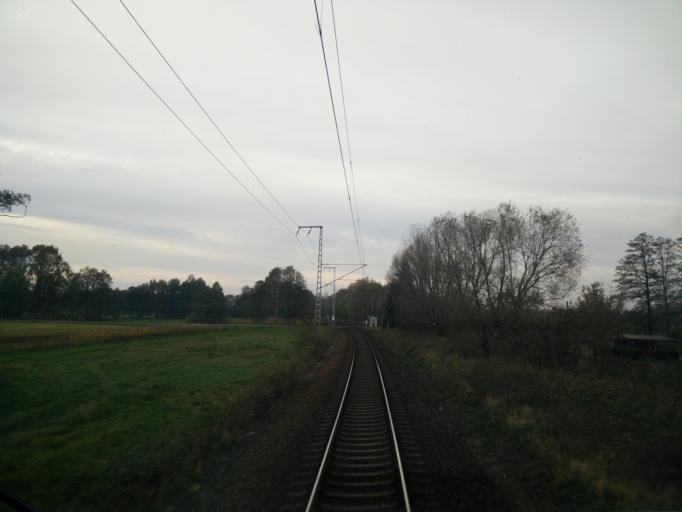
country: DE
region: Brandenburg
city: Lubbenau
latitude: 51.8533
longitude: 13.9813
